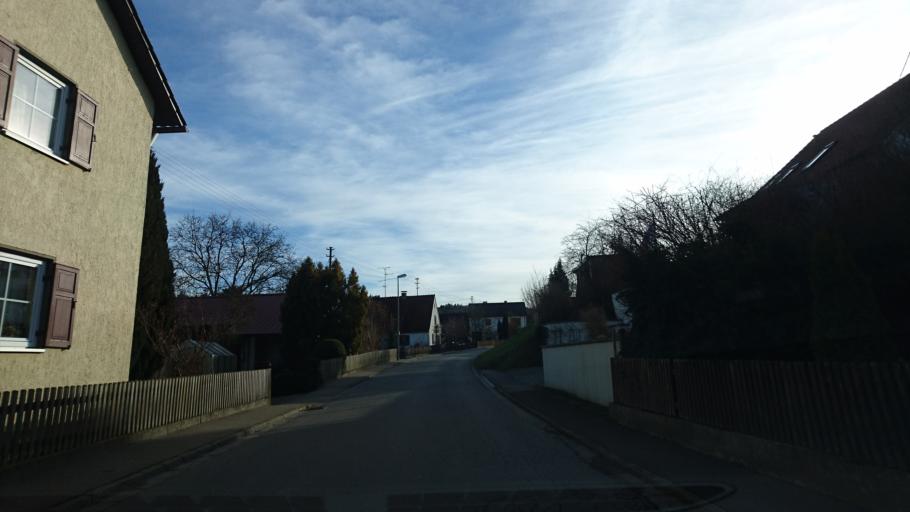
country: DE
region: Bavaria
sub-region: Swabia
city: Altenmunster
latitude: 48.4604
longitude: 10.5954
